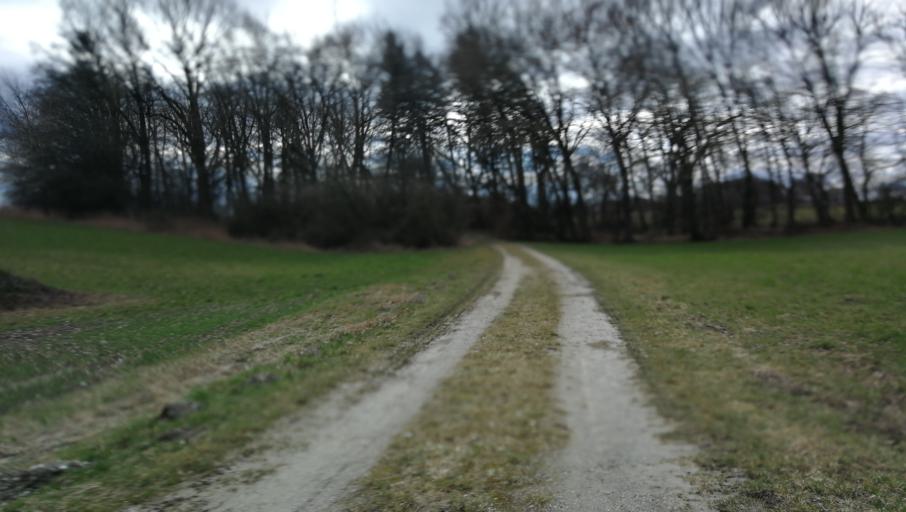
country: DE
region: Bavaria
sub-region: Upper Bavaria
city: Fuerstenfeldbruck
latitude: 48.1963
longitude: 11.2261
